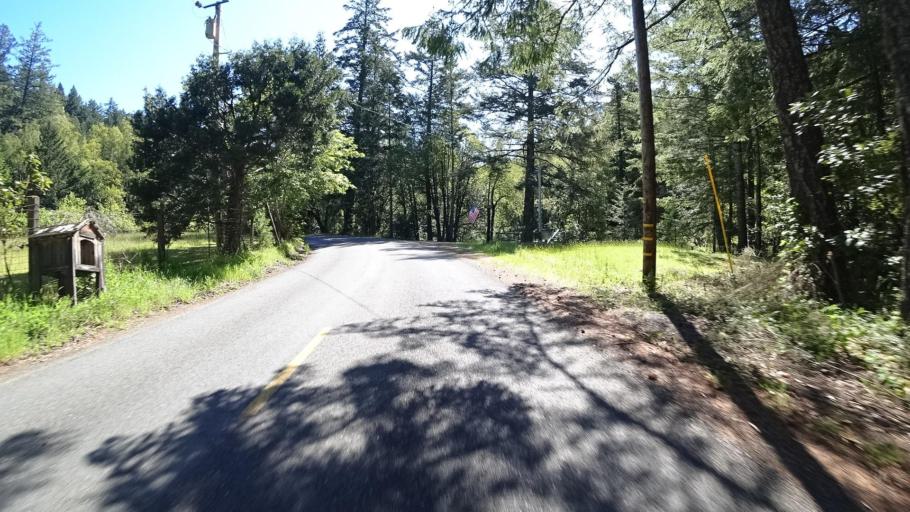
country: US
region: California
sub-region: Humboldt County
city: Rio Dell
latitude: 40.2686
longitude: -124.2234
